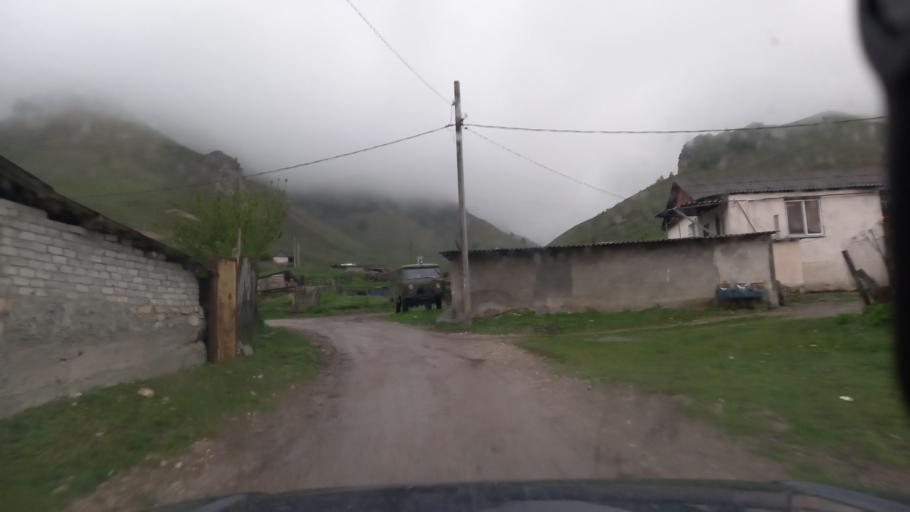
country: RU
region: Kabardino-Balkariya
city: Zhankhoteko
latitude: 43.5116
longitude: 43.1540
